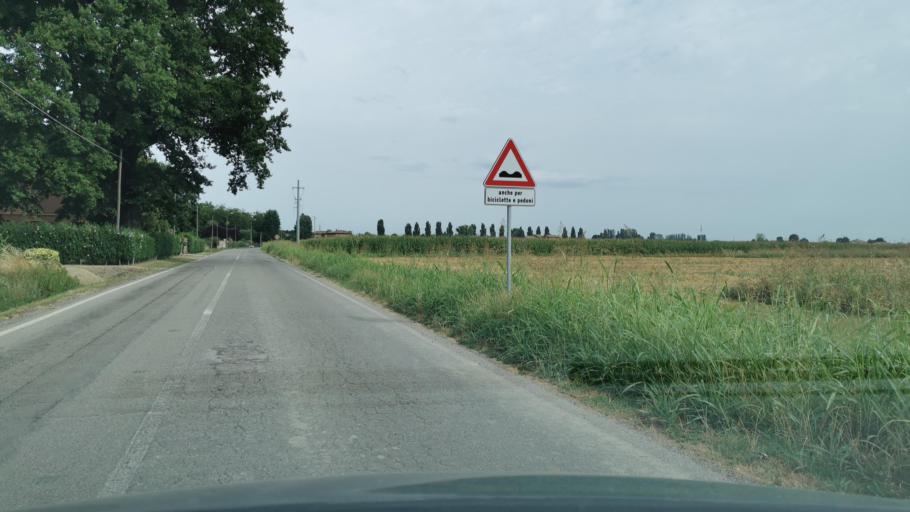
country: IT
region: Emilia-Romagna
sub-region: Provincia di Modena
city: Villanova
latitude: 44.7029
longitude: 10.9076
